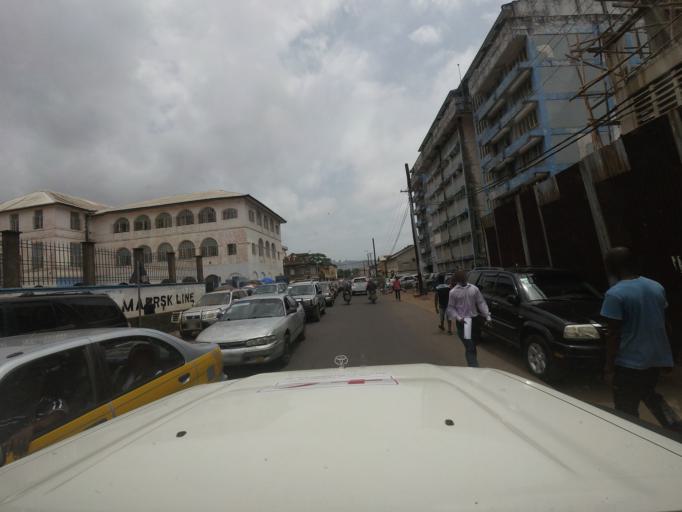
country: SL
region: Western Area
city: Freetown
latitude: 8.4870
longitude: -13.2389
